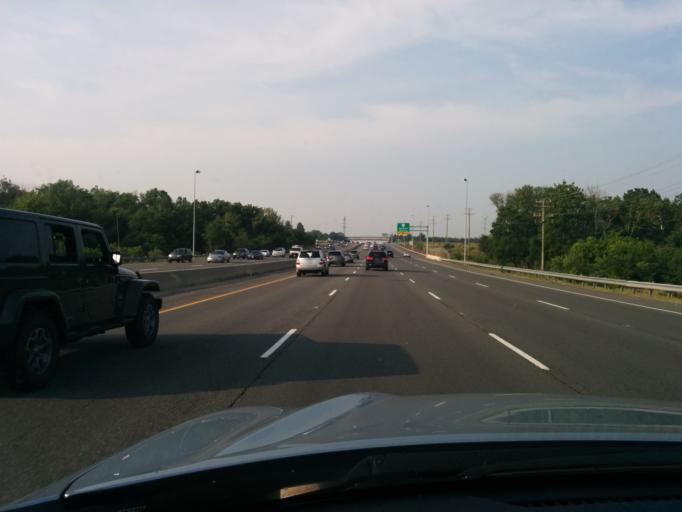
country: US
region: Virginia
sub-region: Loudoun County
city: Sterling
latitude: 39.0184
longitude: -77.4321
